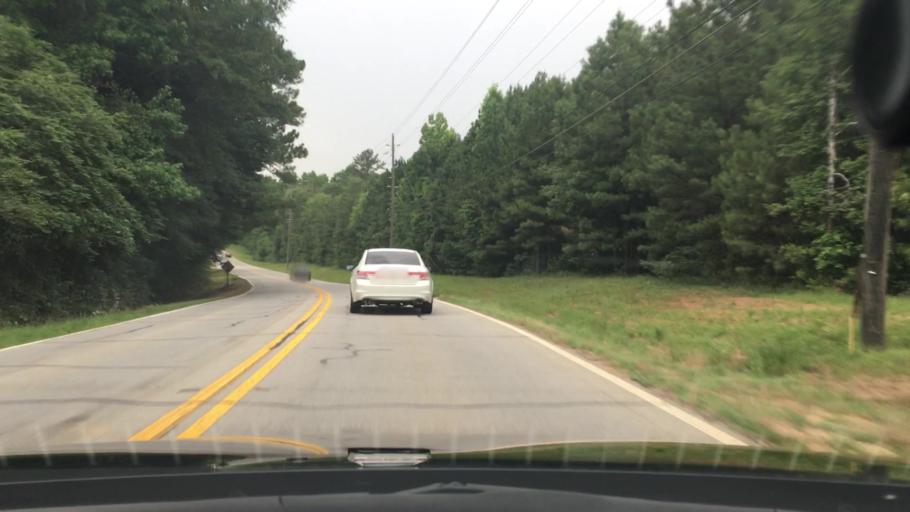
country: US
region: Georgia
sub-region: Coweta County
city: East Newnan
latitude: 33.3550
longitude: -84.7054
